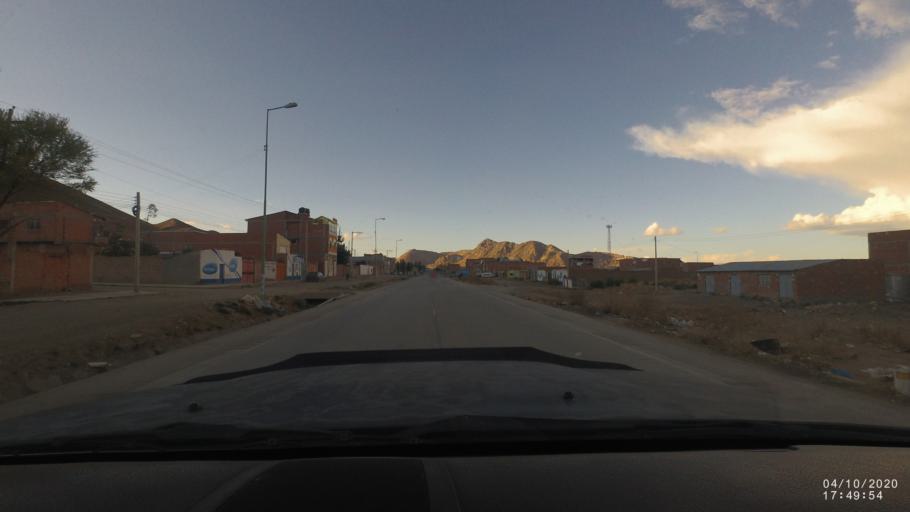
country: BO
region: Oruro
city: Oruro
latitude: -18.0057
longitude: -67.1360
